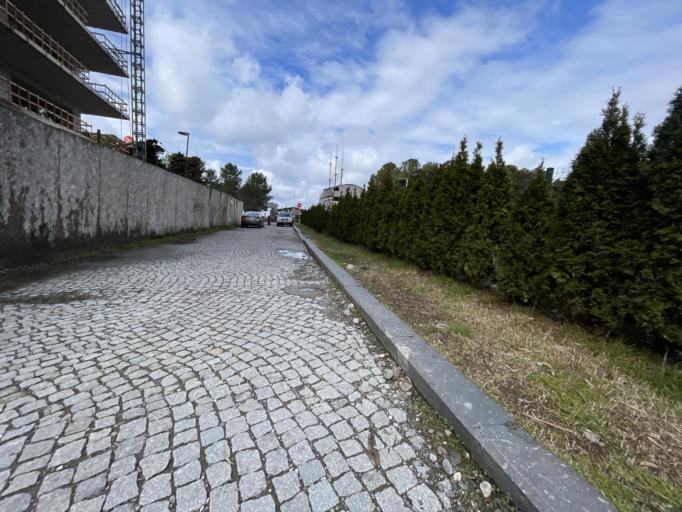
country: GE
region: Ajaria
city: Batumi
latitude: 41.6554
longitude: 41.6363
